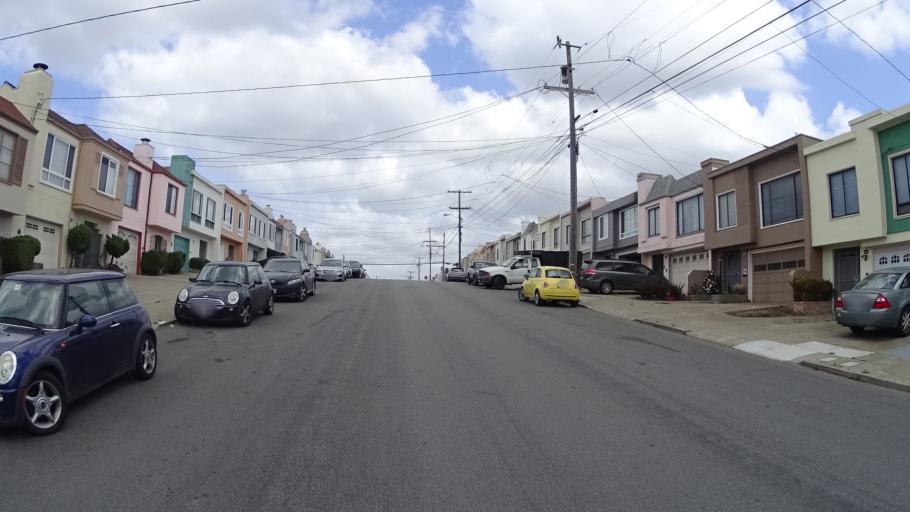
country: US
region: California
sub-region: San Mateo County
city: Daly City
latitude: 37.7428
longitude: -122.4983
